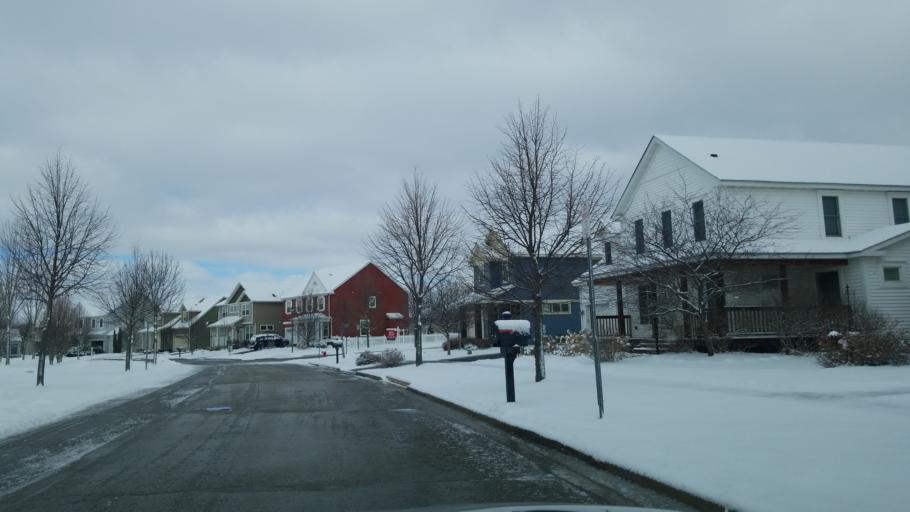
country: US
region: Wisconsin
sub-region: Saint Croix County
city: Hudson
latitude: 44.9530
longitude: -92.6981
